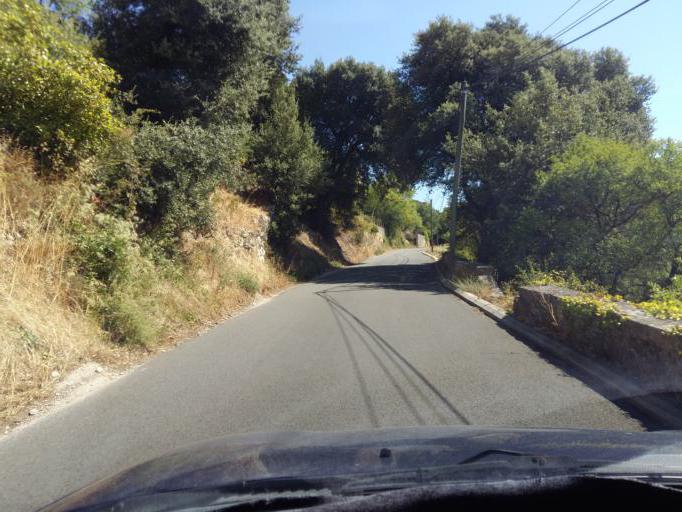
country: FR
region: Provence-Alpes-Cote d'Azur
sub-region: Departement du Vaucluse
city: Venasque
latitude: 43.9950
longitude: 5.1466
